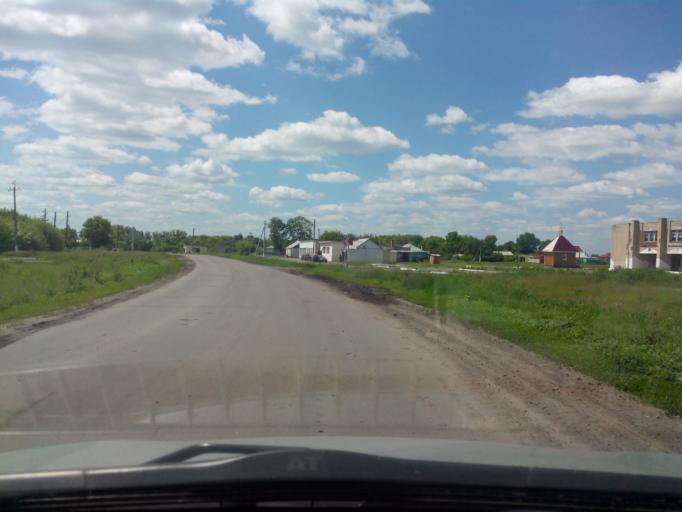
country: RU
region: Voronezj
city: Gribanovskiy
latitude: 51.6290
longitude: 41.9066
